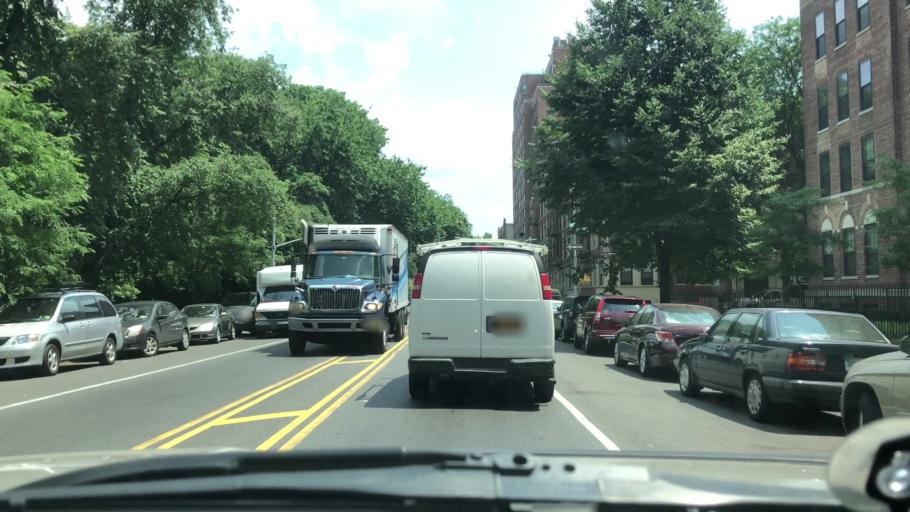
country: US
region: New York
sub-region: Kings County
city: Brooklyn
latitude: 40.6537
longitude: -73.9647
